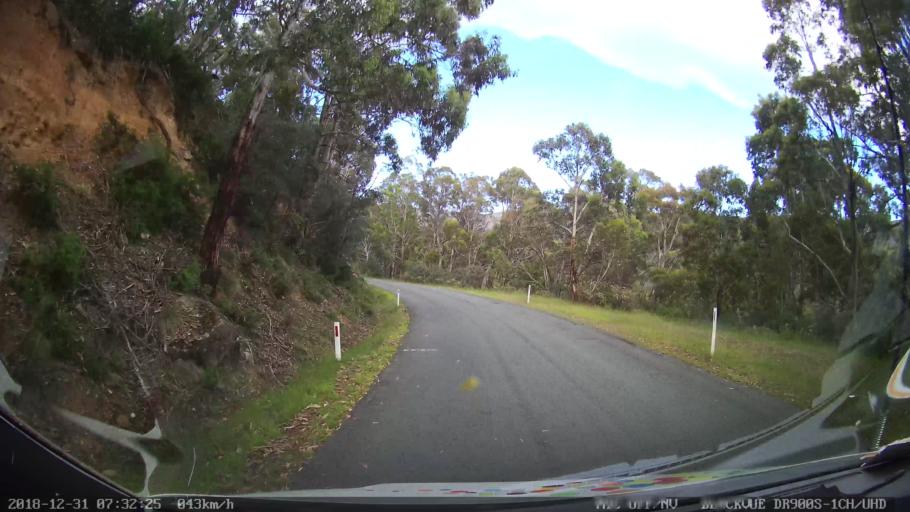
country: AU
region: New South Wales
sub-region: Snowy River
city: Jindabyne
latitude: -36.3303
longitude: 148.4655
